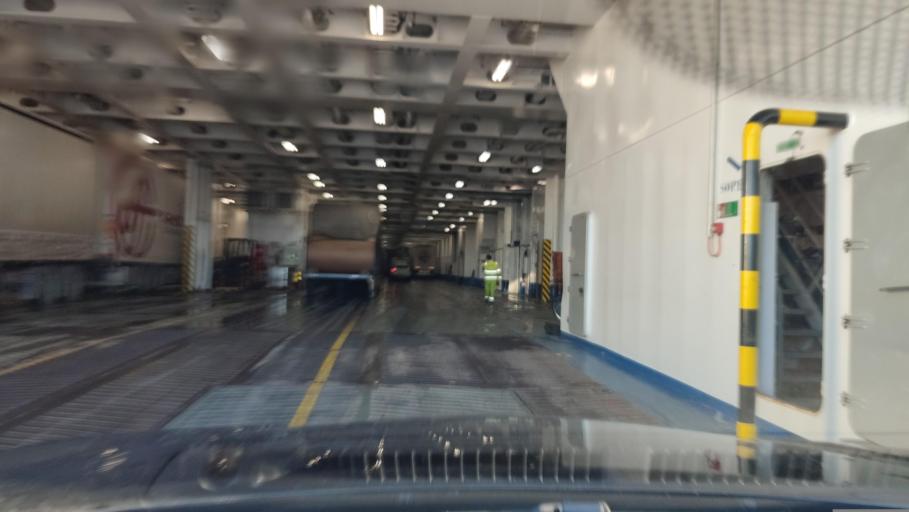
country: SE
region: Vaesterbotten
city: Obbola
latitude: 63.6814
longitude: 20.3412
